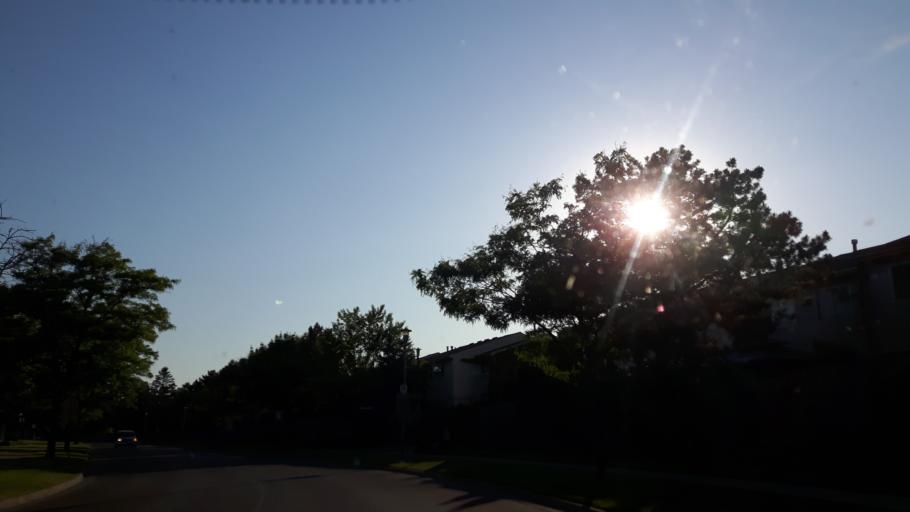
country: CA
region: Ontario
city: London
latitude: 42.9437
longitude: -81.2093
